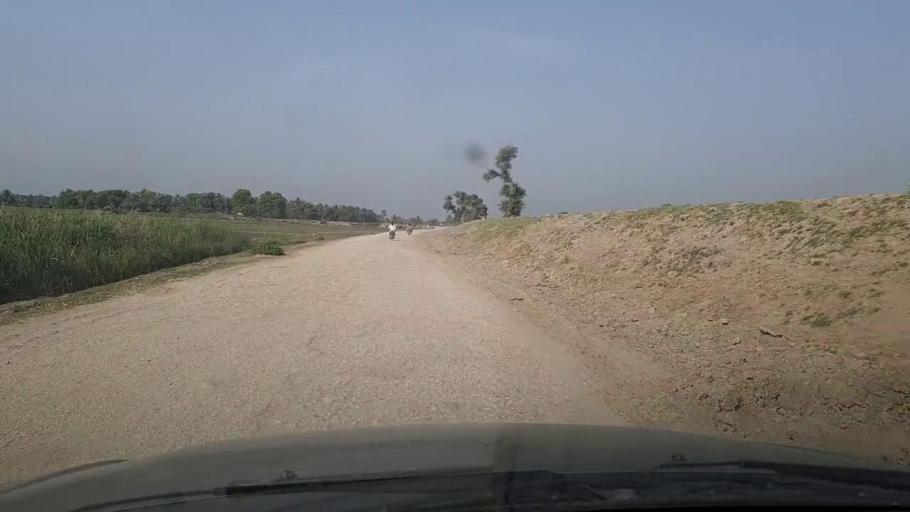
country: PK
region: Sindh
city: Pir jo Goth
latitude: 27.5346
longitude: 68.5107
